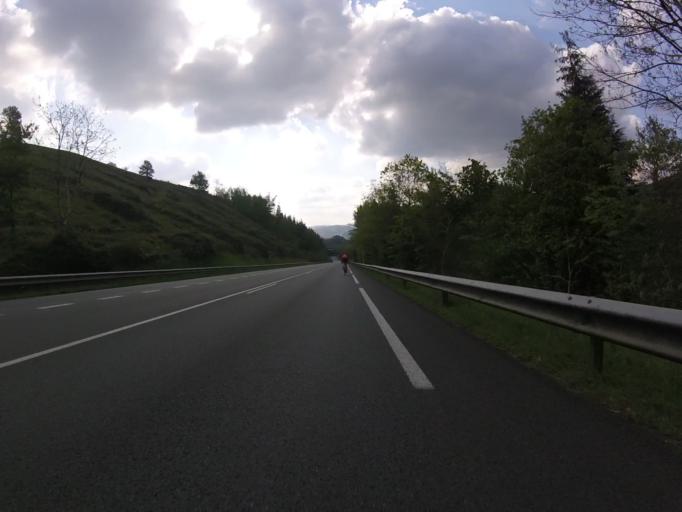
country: ES
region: Basque Country
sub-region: Provincia de Guipuzcoa
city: Azkoitia
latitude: 43.1926
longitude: -2.3341
